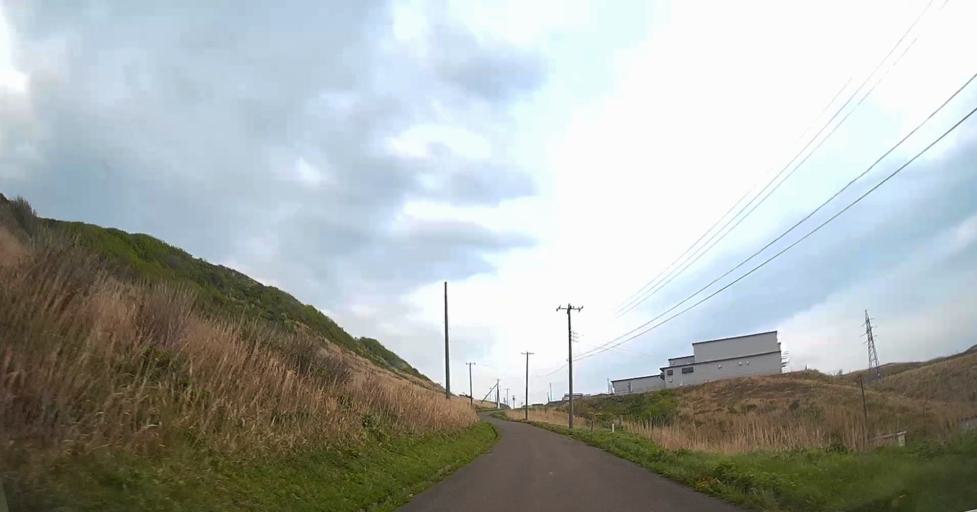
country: JP
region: Aomori
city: Shimokizukuri
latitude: 41.2540
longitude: 140.3428
